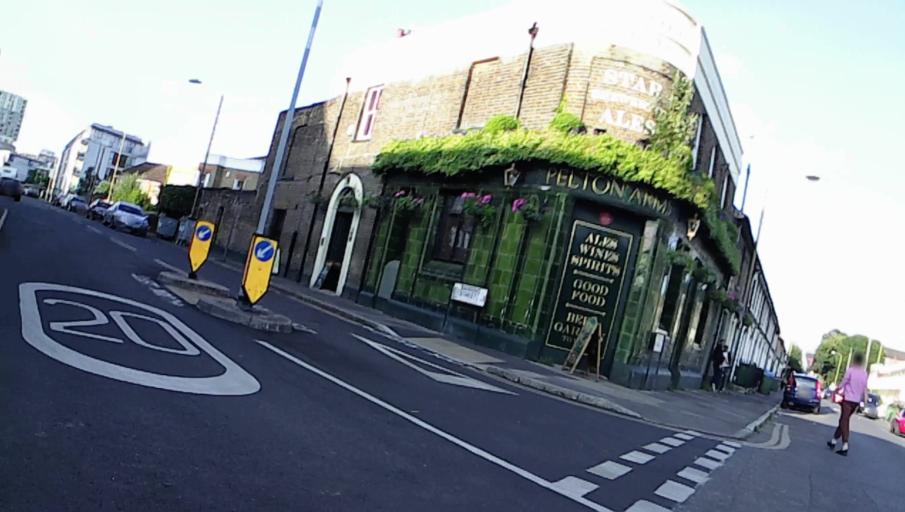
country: GB
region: England
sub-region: Greater London
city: Blackheath
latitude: 51.4869
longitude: 0.0023
